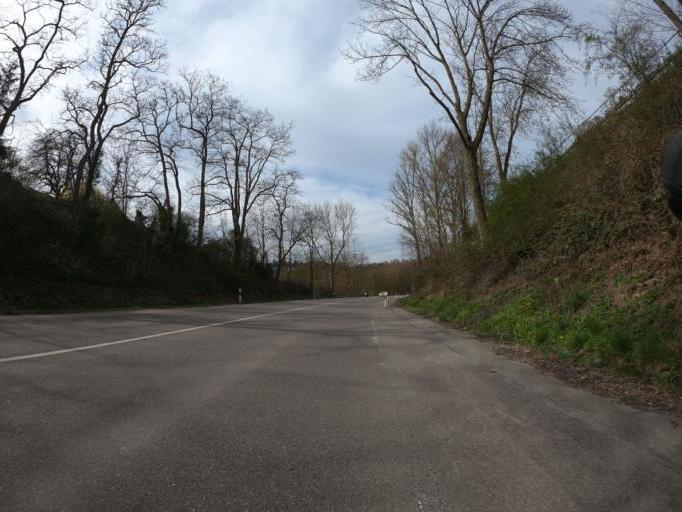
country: DE
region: Baden-Wuerttemberg
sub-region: Regierungsbezirk Stuttgart
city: Ostfildern
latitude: 48.7044
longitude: 9.2163
